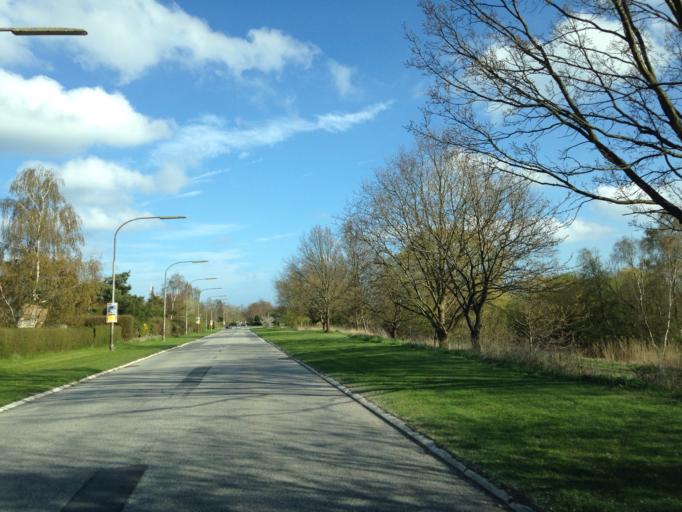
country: DK
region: Zealand
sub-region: Greve Kommune
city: Greve
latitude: 55.5767
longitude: 12.2757
